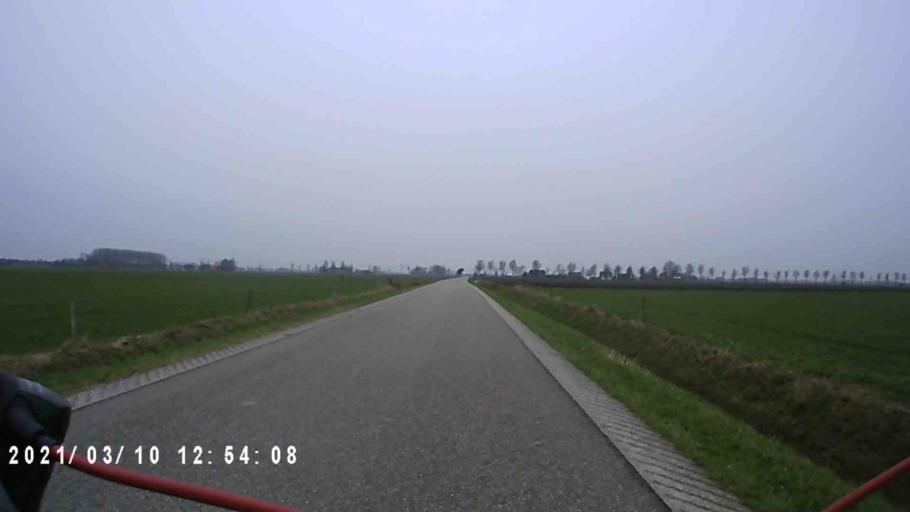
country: NL
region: Groningen
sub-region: Gemeente Bedum
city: Bedum
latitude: 53.2982
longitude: 6.6277
